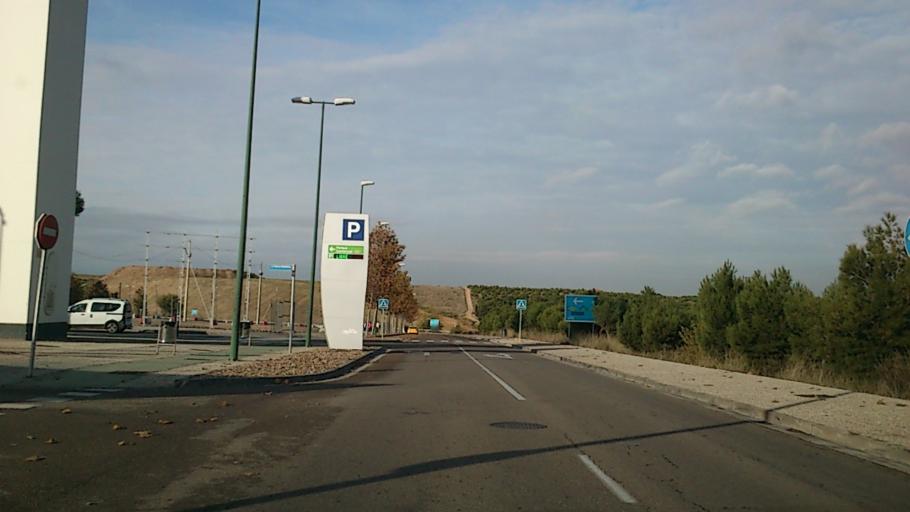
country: ES
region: Aragon
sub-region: Provincia de Zaragoza
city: Delicias
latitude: 41.6114
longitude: -0.8890
